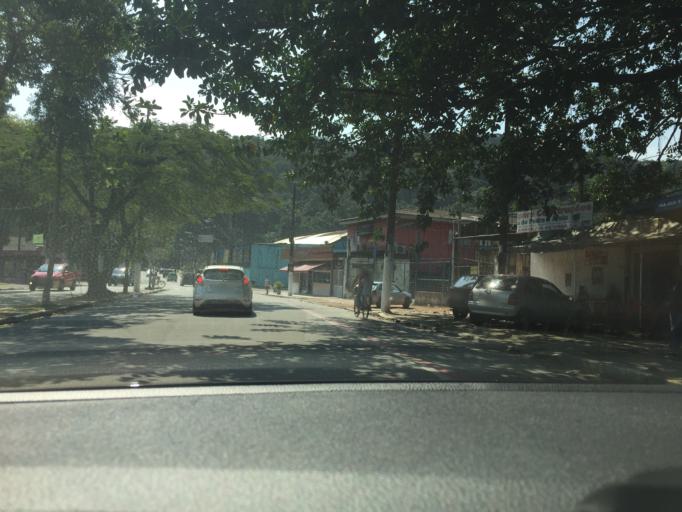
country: BR
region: Sao Paulo
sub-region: Guaruja
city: Guaruja
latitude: -23.9832
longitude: -46.2459
